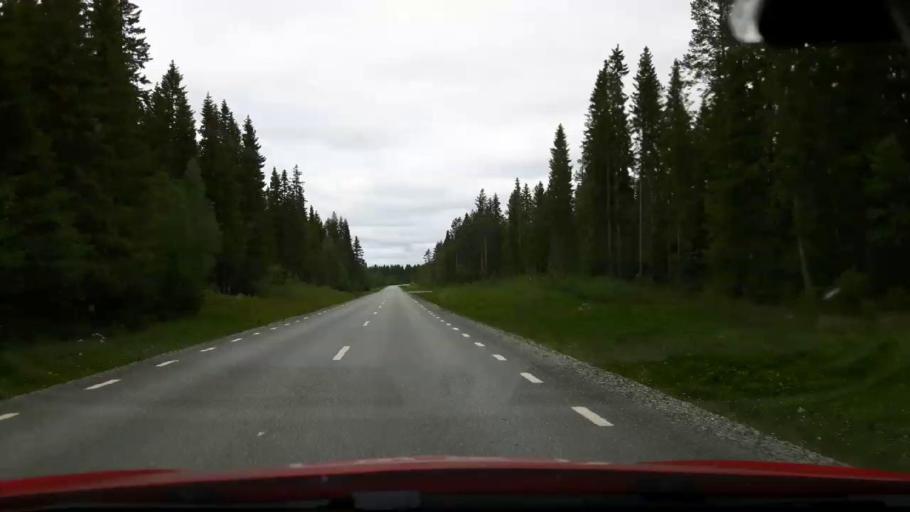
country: SE
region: Jaemtland
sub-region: OEstersunds Kommun
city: Lit
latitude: 63.6794
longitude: 14.6821
